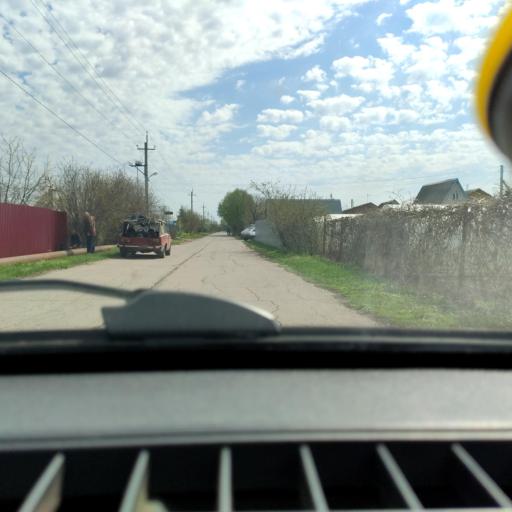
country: RU
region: Samara
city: Tol'yatti
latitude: 53.6994
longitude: 49.4435
